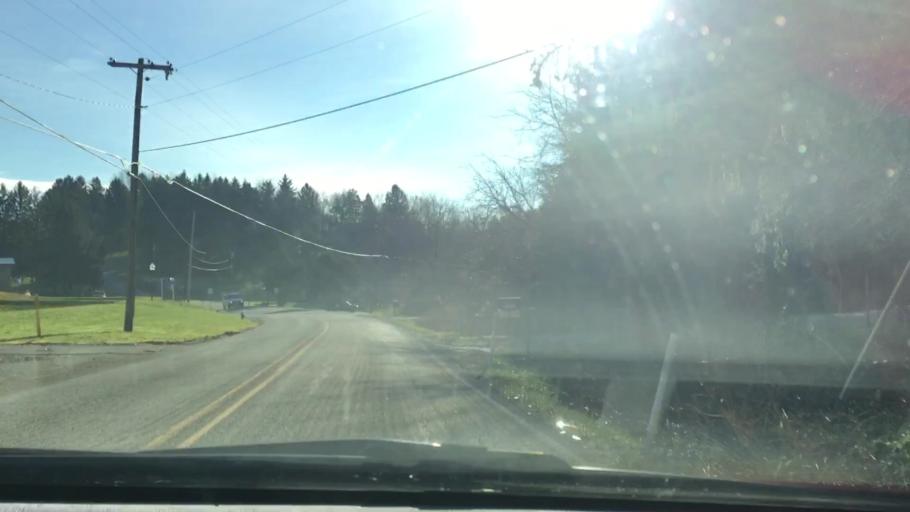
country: US
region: Pennsylvania
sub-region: Westmoreland County
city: Irwin
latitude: 40.3019
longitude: -79.7016
